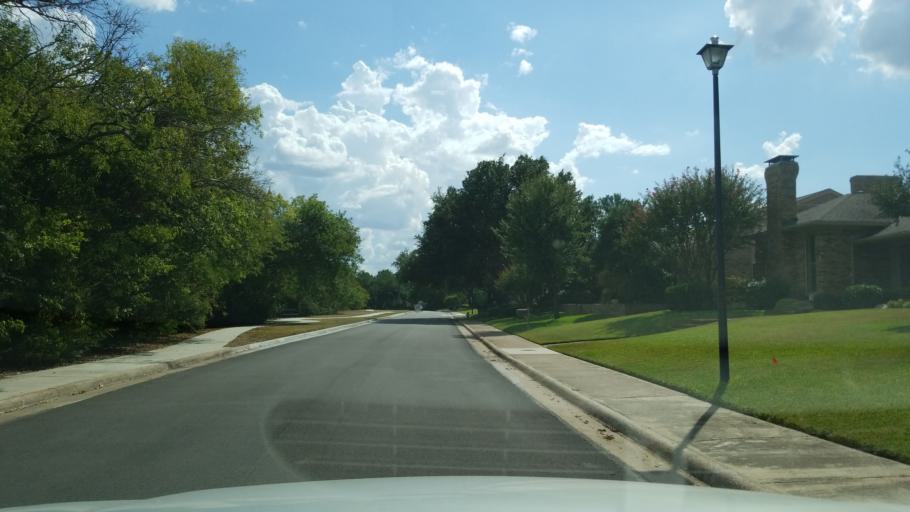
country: US
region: Texas
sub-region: Dallas County
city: Addison
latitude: 32.9564
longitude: -96.7977
